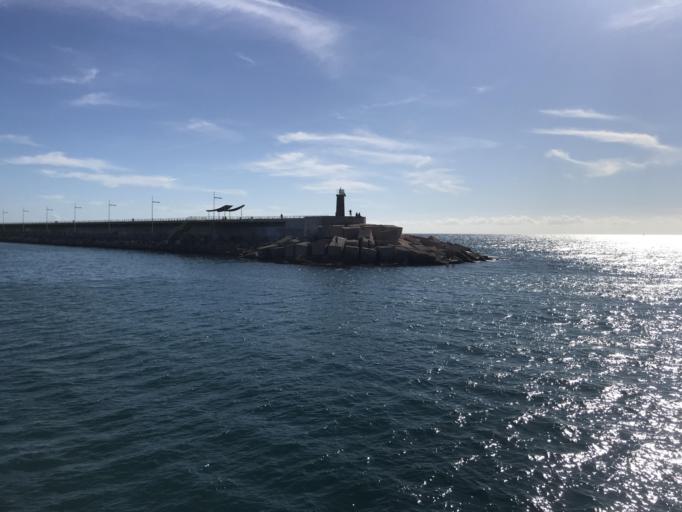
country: ES
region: Valencia
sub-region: Provincia de Alicante
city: Torrevieja
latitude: 37.9647
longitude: -0.6887
